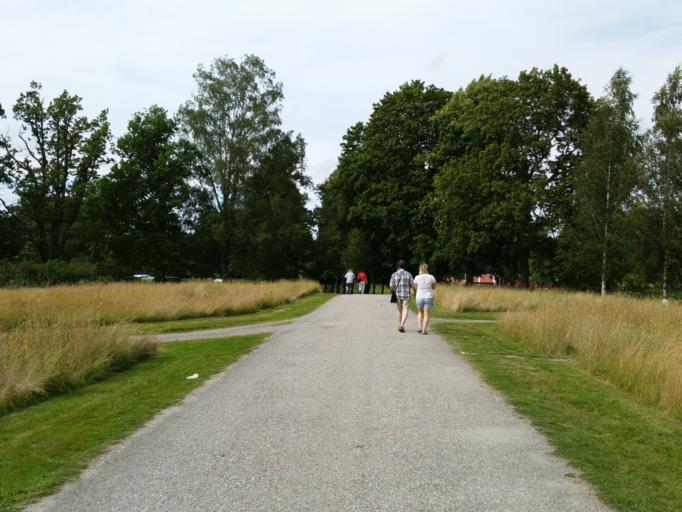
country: SE
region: Soedermanland
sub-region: Strangnas Kommun
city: Mariefred
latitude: 59.2570
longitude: 17.2179
